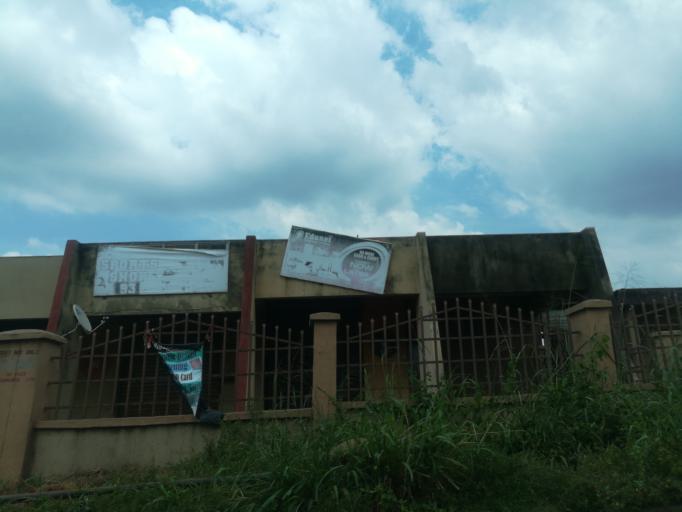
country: NG
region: Oyo
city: Ibadan
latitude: 7.3983
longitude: 3.8836
